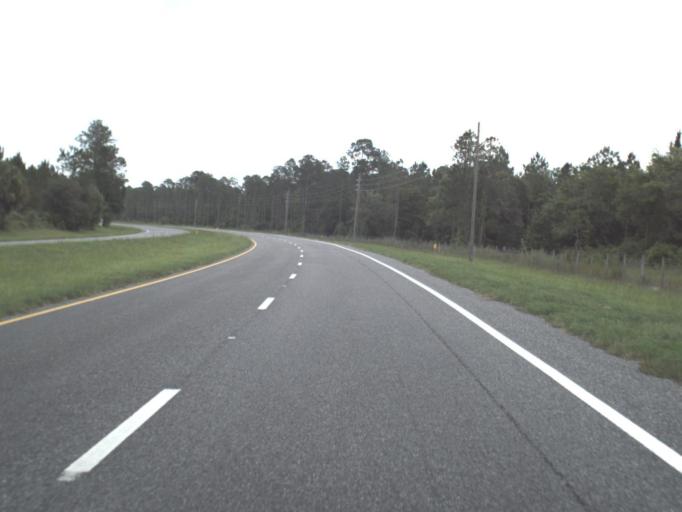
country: US
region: Florida
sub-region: Clay County
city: Middleburg
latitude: 29.9789
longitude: -81.9283
